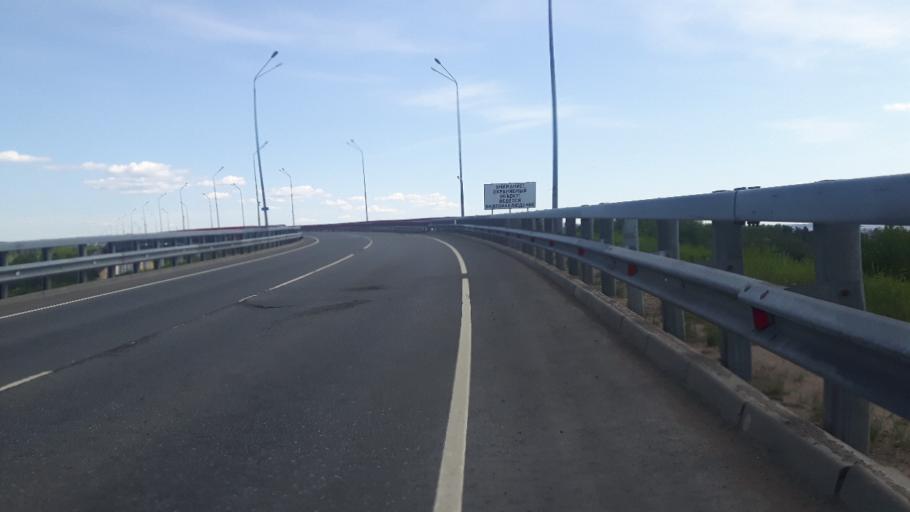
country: RU
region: Leningrad
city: Vyborg
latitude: 60.7392
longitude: 28.6845
